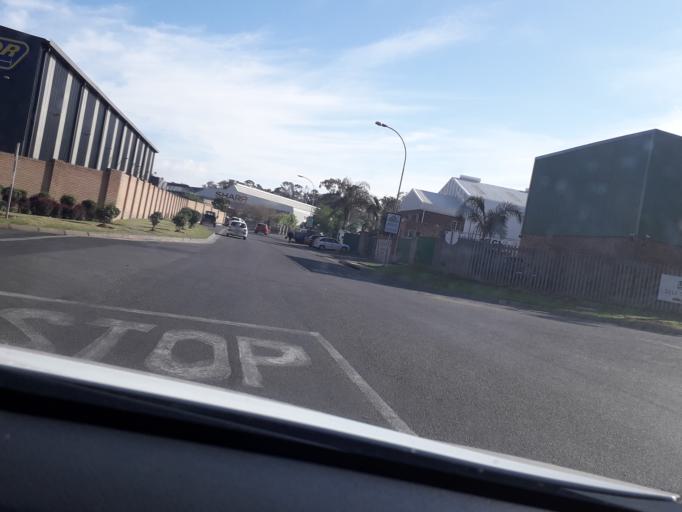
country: ZA
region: Gauteng
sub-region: City of Johannesburg Metropolitan Municipality
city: Modderfontein
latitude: -26.1594
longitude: 28.1831
